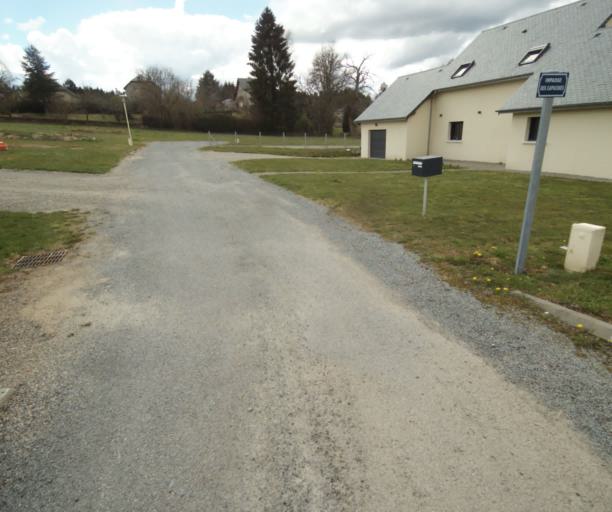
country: FR
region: Limousin
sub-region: Departement de la Correze
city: Correze
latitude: 45.3365
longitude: 1.9435
